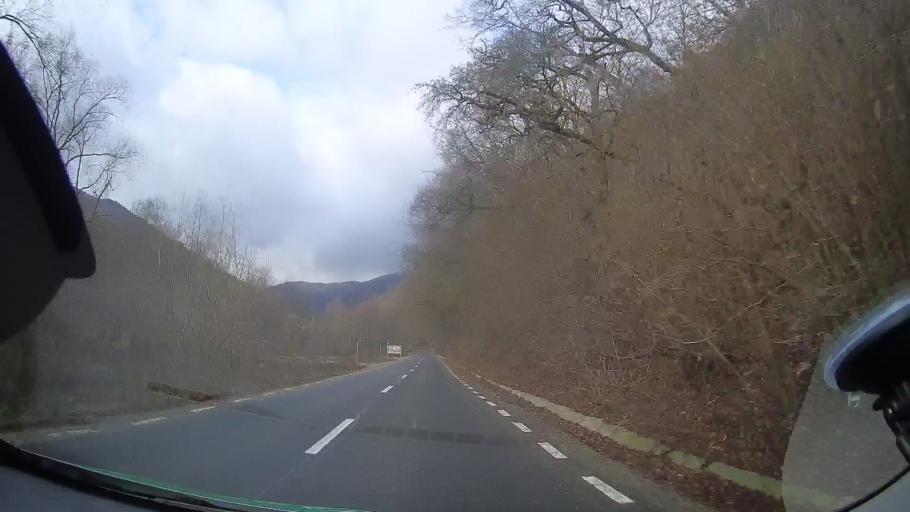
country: RO
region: Cluj
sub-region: Comuna Valea Ierii
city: Valea Ierii
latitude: 46.6373
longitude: 23.3676
